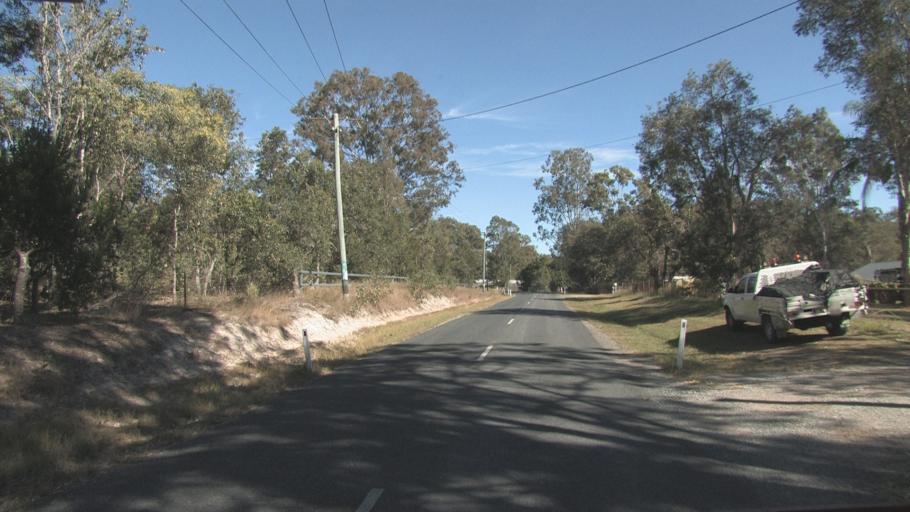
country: AU
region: Queensland
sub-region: Ipswich
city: Springfield Lakes
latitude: -27.7173
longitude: 152.9389
